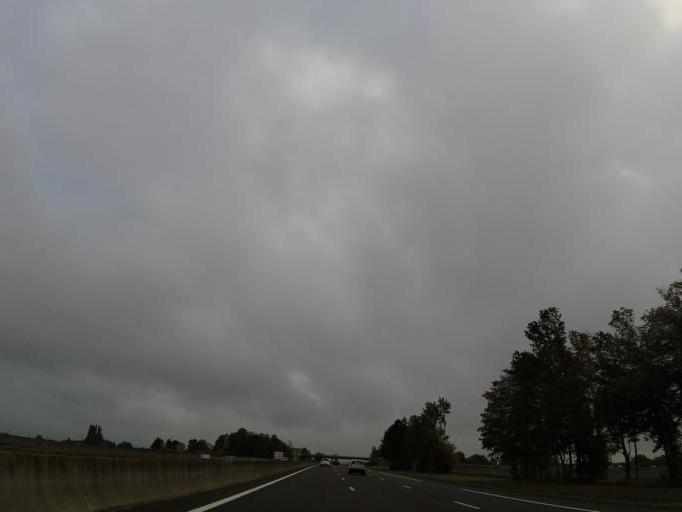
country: FR
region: Ile-de-France
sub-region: Departement de Seine-et-Marne
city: Bailly-Romainvilliers
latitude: 48.8575
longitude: 2.8415
